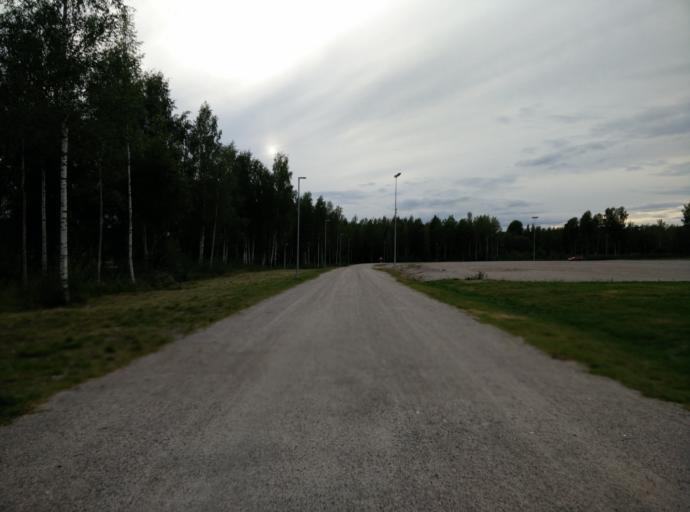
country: FI
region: Haeme
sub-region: Haemeenlinna
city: Haemeenlinna
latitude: 60.9846
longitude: 24.4837
